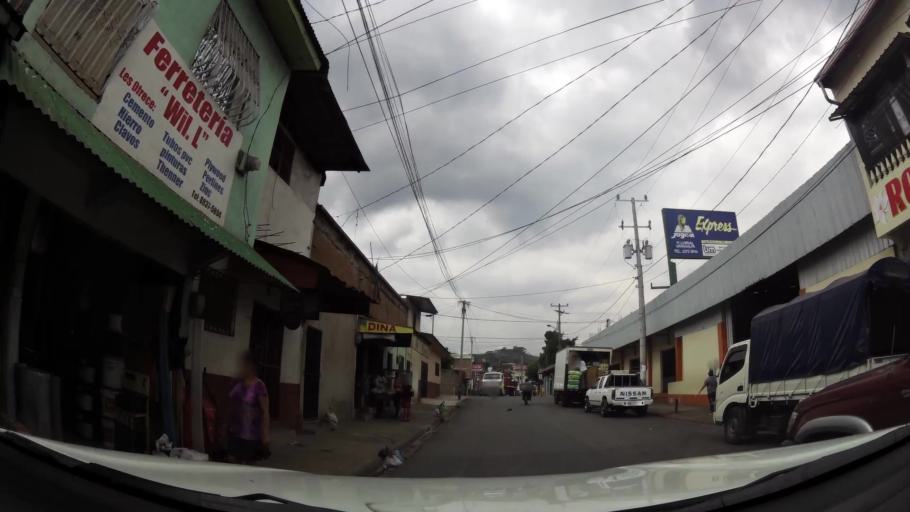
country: NI
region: Matagalpa
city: Matagalpa
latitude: 12.9204
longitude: -85.9252
